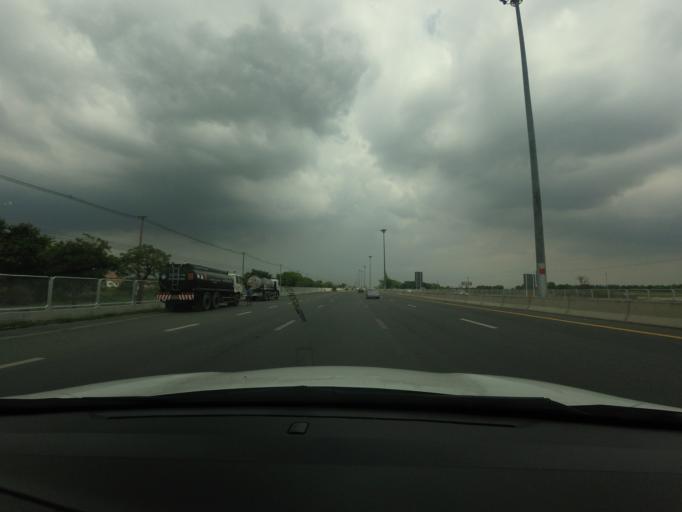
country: TH
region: Phra Nakhon Si Ayutthaya
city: Wang Noi
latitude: 14.1653
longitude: 100.6504
